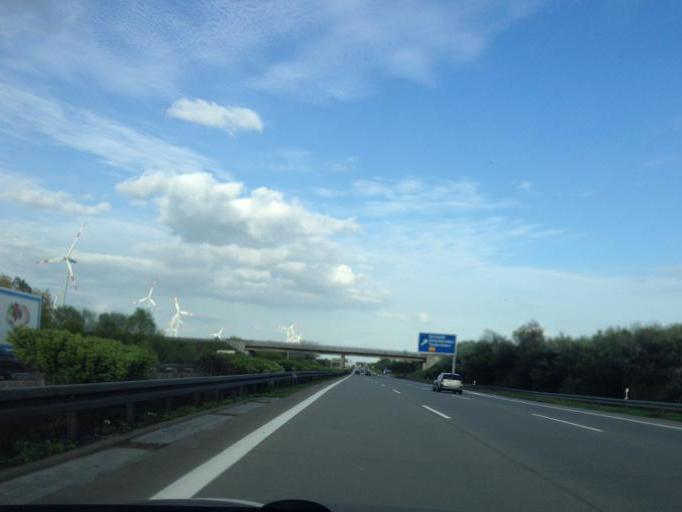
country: DE
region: Saxony-Anhalt
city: Eichenbarleben
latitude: 52.1870
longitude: 11.3599
